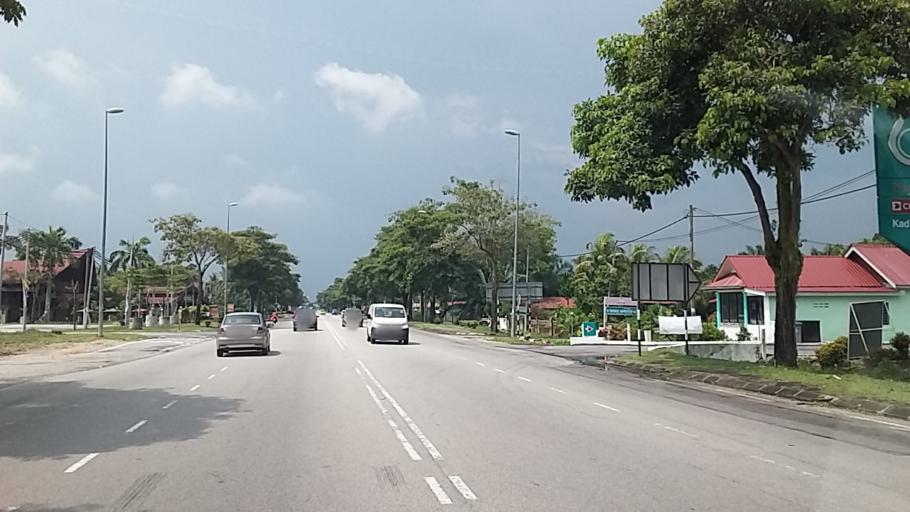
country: MY
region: Johor
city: Parit Raja
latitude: 1.8611
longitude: 103.1051
